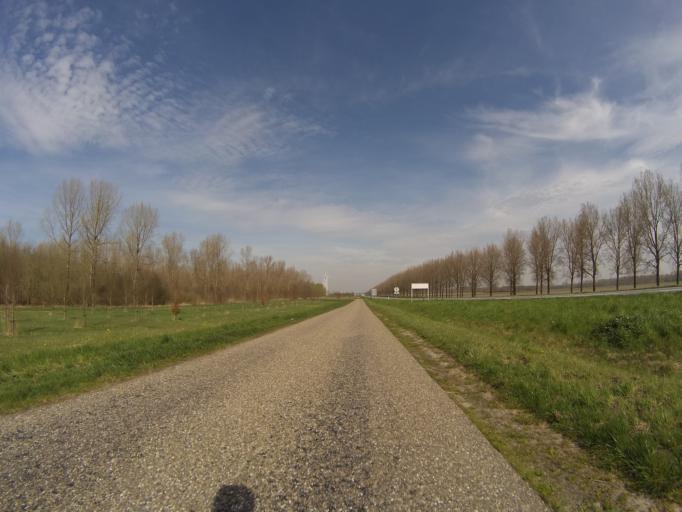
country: NL
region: Gelderland
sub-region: Gemeente Nijkerk
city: Nijkerk
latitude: 52.2687
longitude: 5.4678
